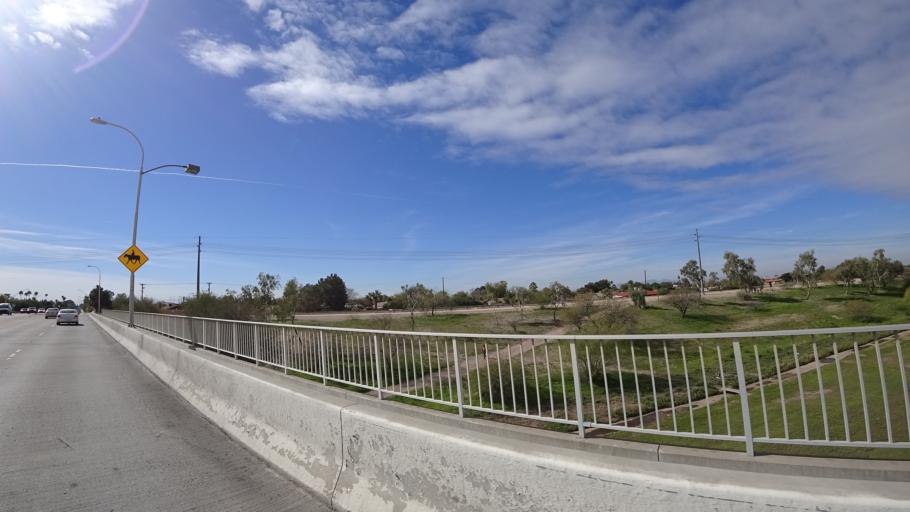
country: US
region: Arizona
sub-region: Maricopa County
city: Peoria
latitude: 33.6070
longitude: -112.1860
